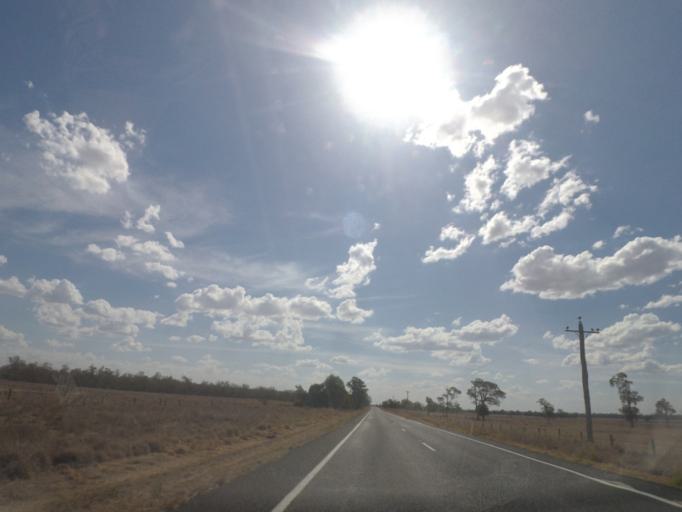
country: AU
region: Queensland
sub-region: Southern Downs
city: Stanthorpe
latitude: -28.4143
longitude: 151.1534
